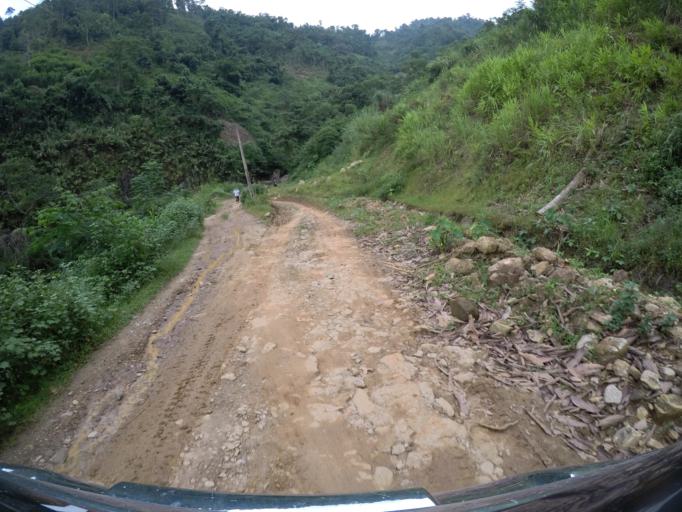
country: VN
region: Yen Bai
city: Son Thinh
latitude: 21.6789
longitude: 104.5830
